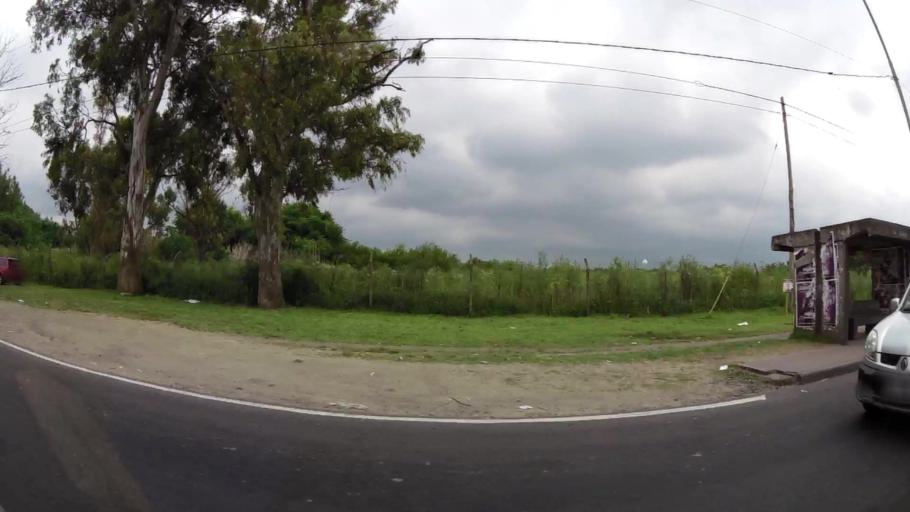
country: AR
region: Buenos Aires
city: San Justo
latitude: -34.7061
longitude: -58.5331
